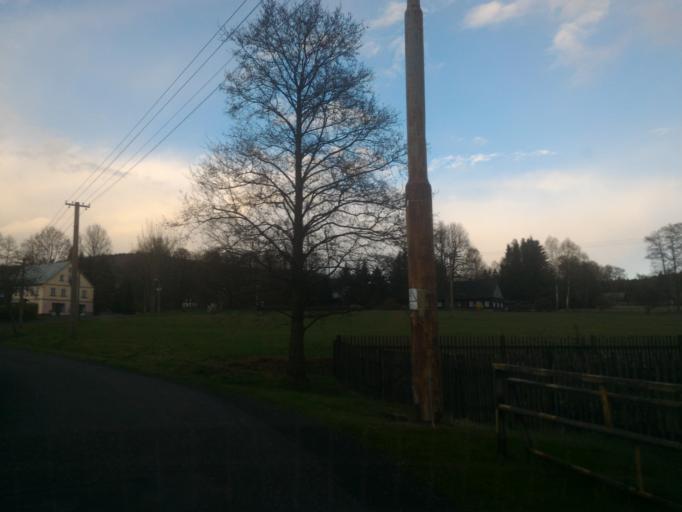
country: CZ
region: Ustecky
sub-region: Okres Decin
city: Chribska
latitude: 50.8880
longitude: 14.4635
